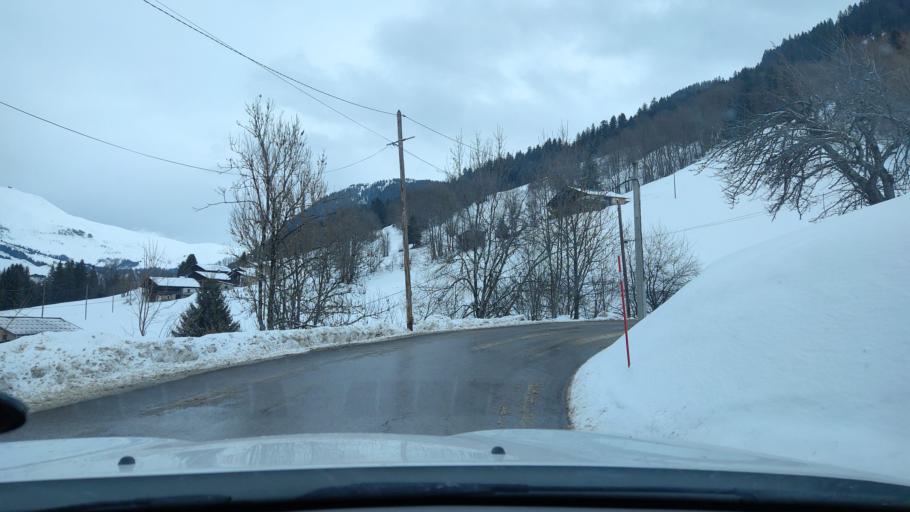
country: FR
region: Rhone-Alpes
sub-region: Departement de la Savoie
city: Beaufort
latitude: 45.7500
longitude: 6.5949
